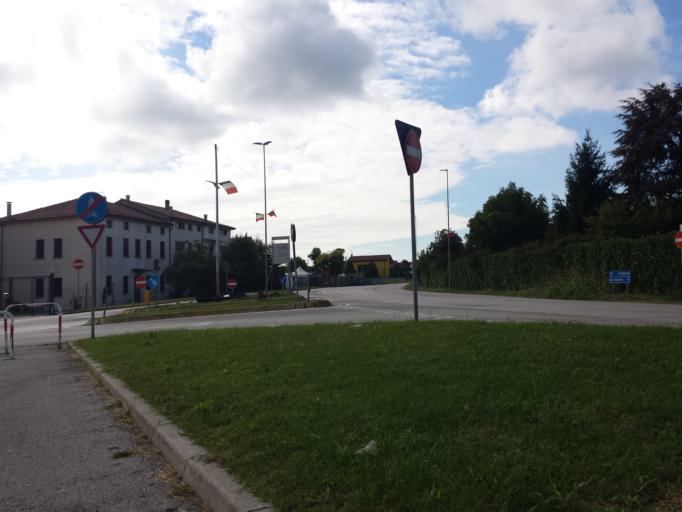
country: IT
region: Veneto
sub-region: Provincia di Vicenza
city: Sandrigo
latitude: 45.6578
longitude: 11.5923
